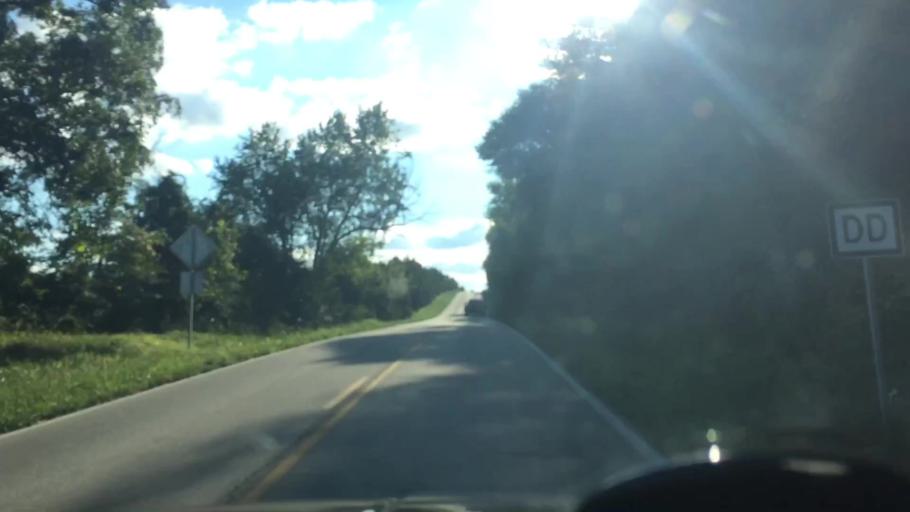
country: US
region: Missouri
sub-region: Greene County
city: Strafford
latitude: 37.2856
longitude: -93.0948
